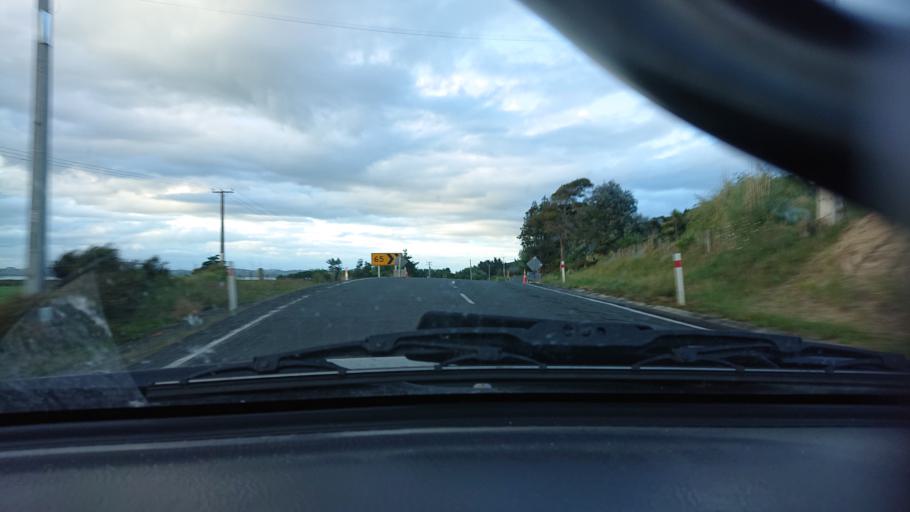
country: NZ
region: Auckland
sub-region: Auckland
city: Wellsford
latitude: -36.4457
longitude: 174.4327
